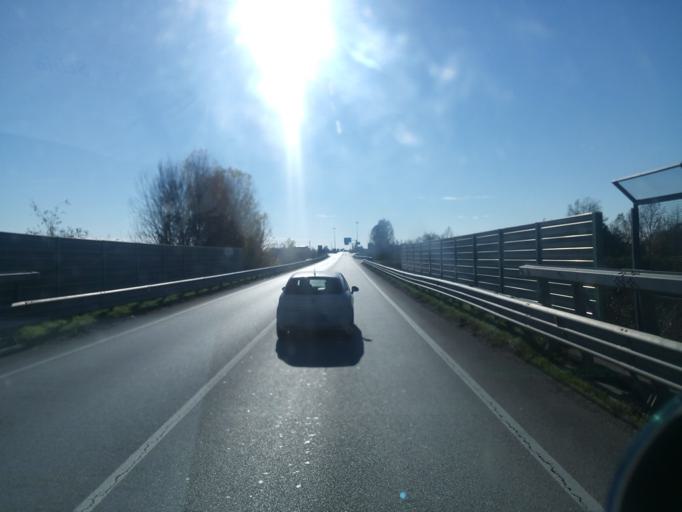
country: IT
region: Veneto
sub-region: Provincia di Padova
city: Loreggia
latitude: 45.5912
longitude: 11.9564
